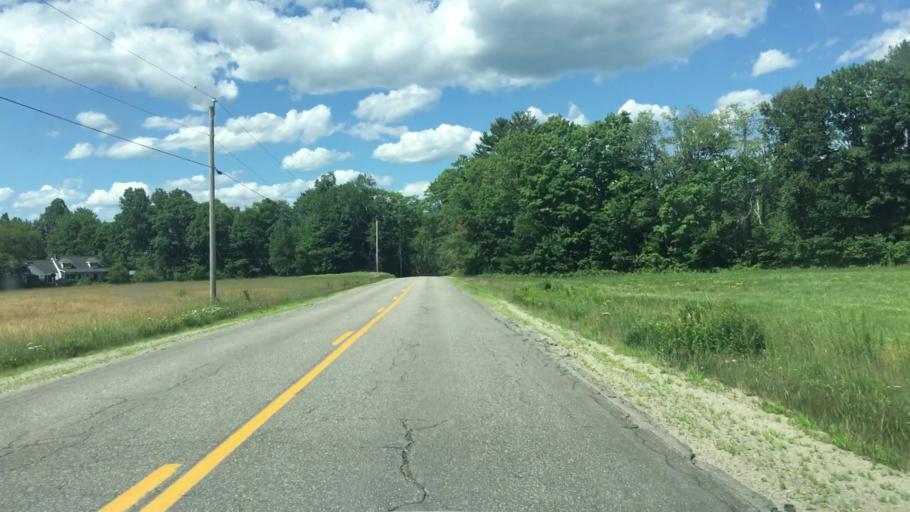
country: US
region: Maine
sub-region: Franklin County
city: Chesterville
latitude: 44.5846
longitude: -70.0891
